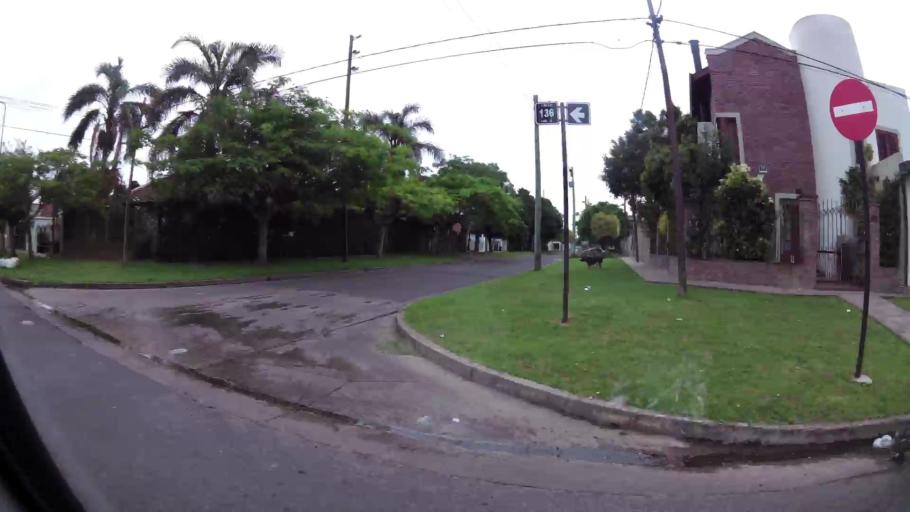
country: AR
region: Buenos Aires
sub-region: Partido de La Plata
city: La Plata
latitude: -34.9272
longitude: -58.0003
